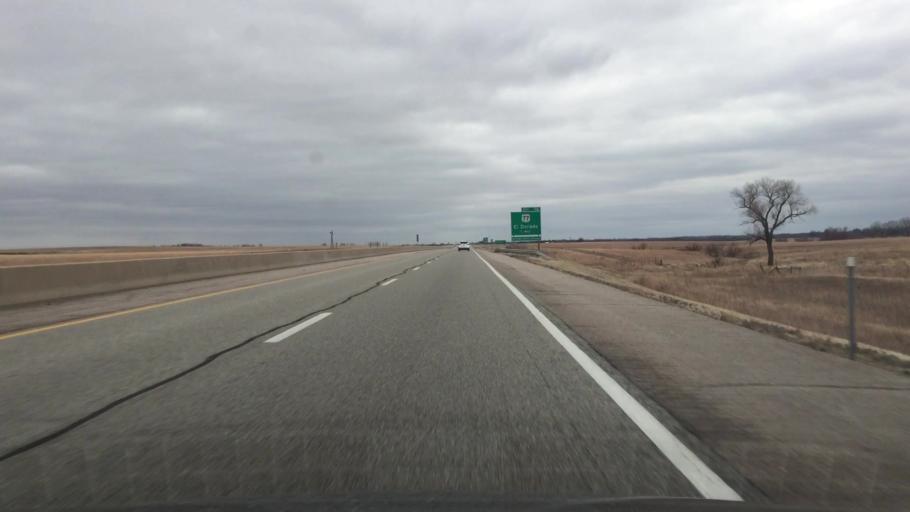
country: US
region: Kansas
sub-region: Butler County
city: El Dorado
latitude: 37.8946
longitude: -96.8357
